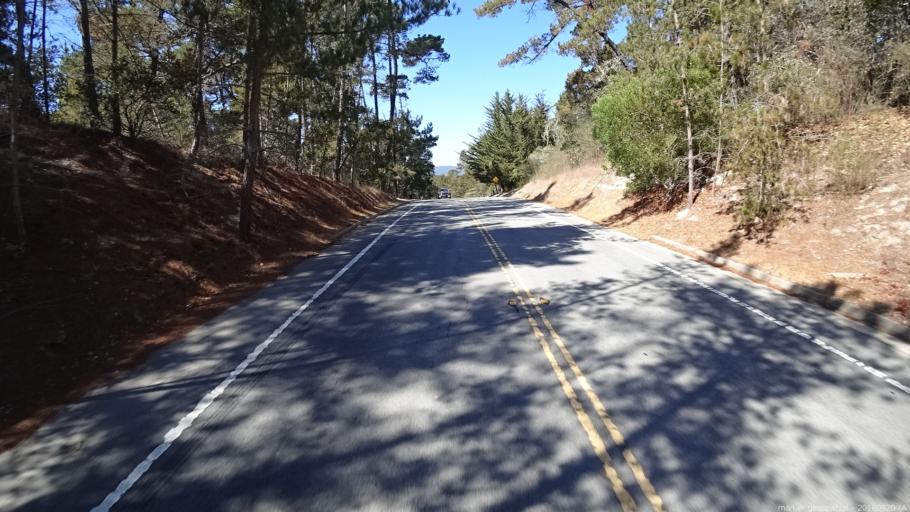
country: US
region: California
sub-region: Monterey County
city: Del Rey Oaks
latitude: 36.5743
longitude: -121.8590
